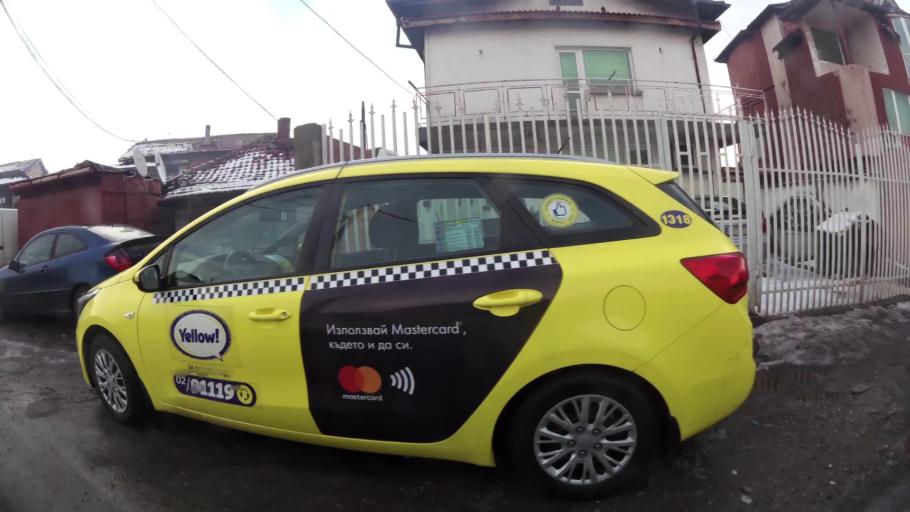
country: BG
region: Sofia-Capital
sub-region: Stolichna Obshtina
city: Sofia
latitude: 42.6927
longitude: 23.2642
